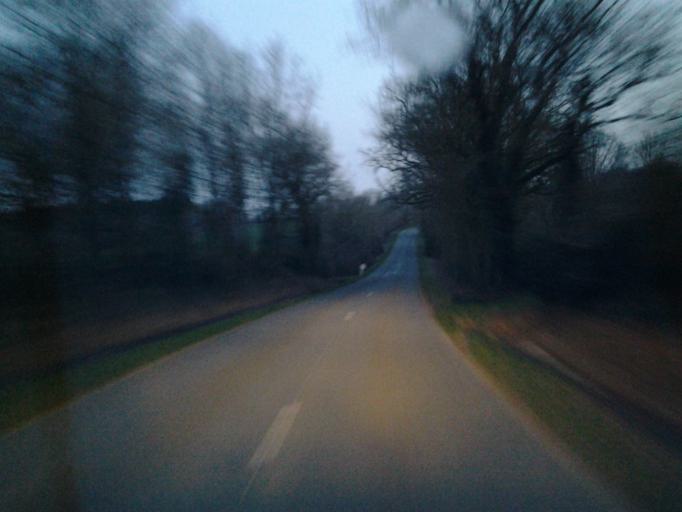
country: FR
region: Pays de la Loire
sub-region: Departement de la Vendee
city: Saint-Florent-des-Bois
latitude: 46.5796
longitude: -1.3549
